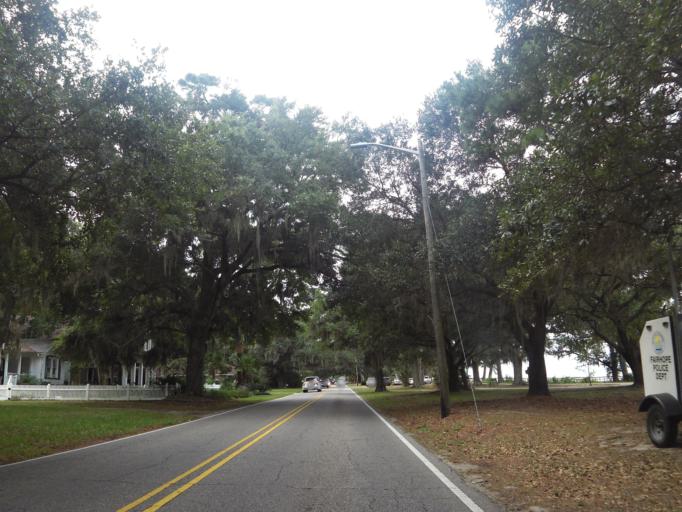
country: US
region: Alabama
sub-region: Baldwin County
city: Fairhope
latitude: 30.5163
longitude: -87.9163
